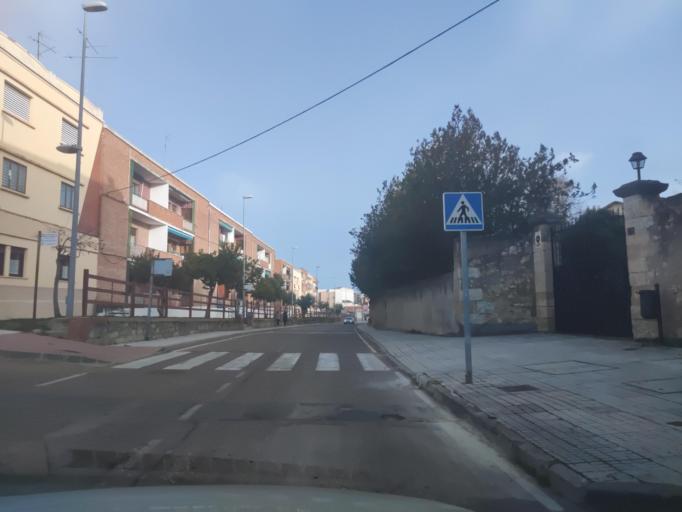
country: ES
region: Castille and Leon
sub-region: Provincia de Salamanca
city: Ciudad Rodrigo
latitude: 40.5974
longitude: -6.5280
